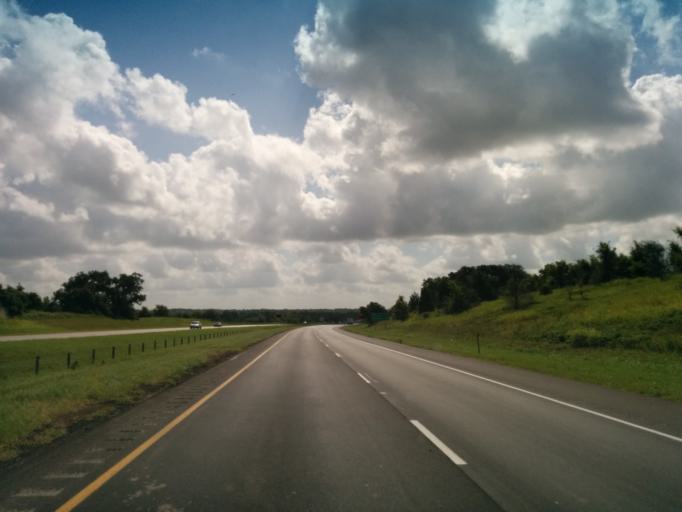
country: US
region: Texas
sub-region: Fayette County
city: Schulenburg
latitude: 29.6955
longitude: -96.8883
